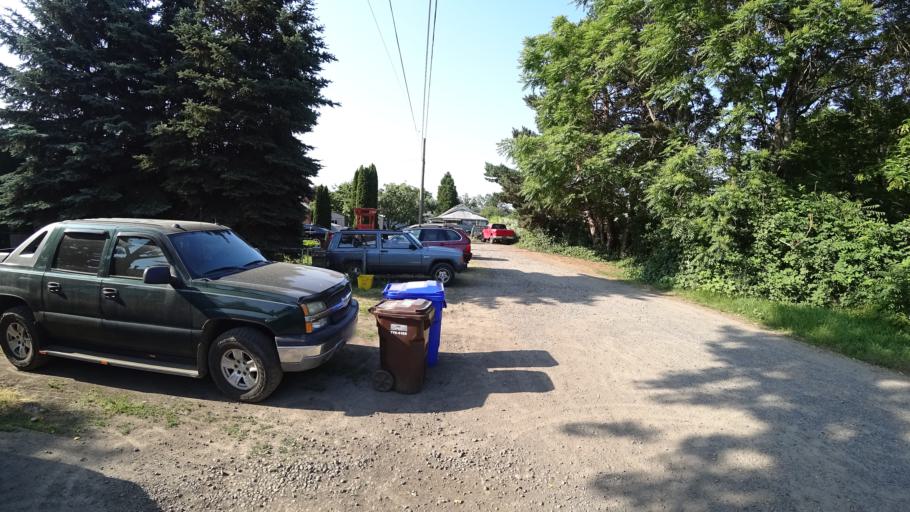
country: US
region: Oregon
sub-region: Multnomah County
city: Lents
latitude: 45.4619
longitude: -122.5861
